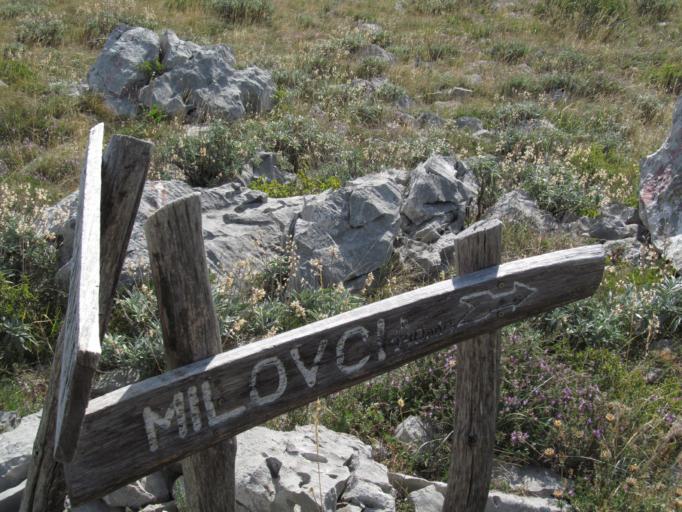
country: HR
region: Zadarska
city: Starigrad
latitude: 44.3368
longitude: 15.4295
